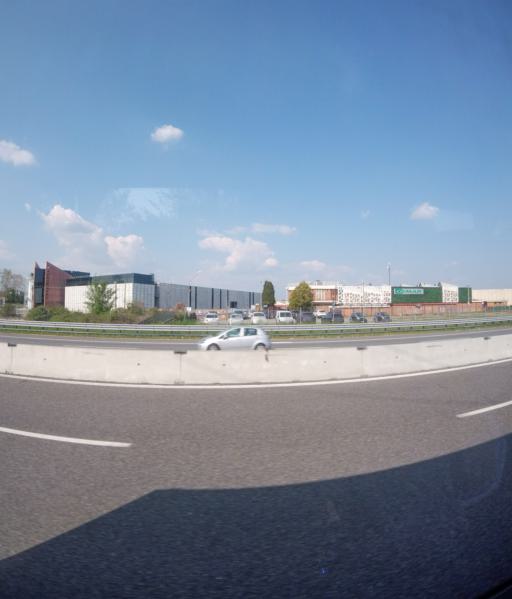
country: IT
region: Lombardy
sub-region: Provincia di Varese
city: Cassano Magnago
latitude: 45.6560
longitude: 8.8189
